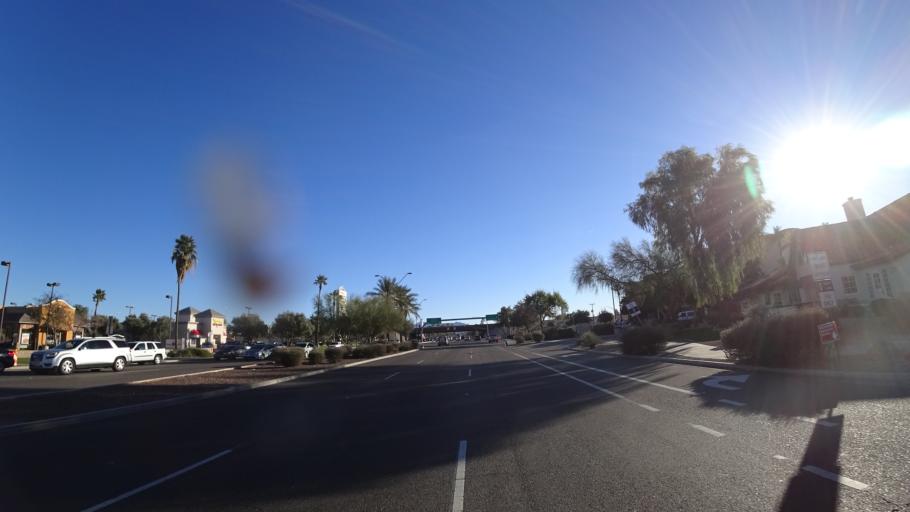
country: US
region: Arizona
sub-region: Maricopa County
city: Avondale
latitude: 33.4601
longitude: -112.3412
